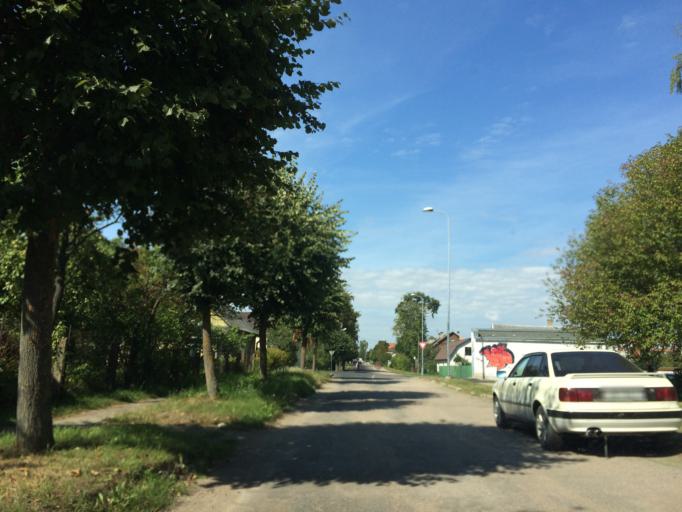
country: LV
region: Rezekne
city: Rezekne
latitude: 56.5146
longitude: 27.3471
